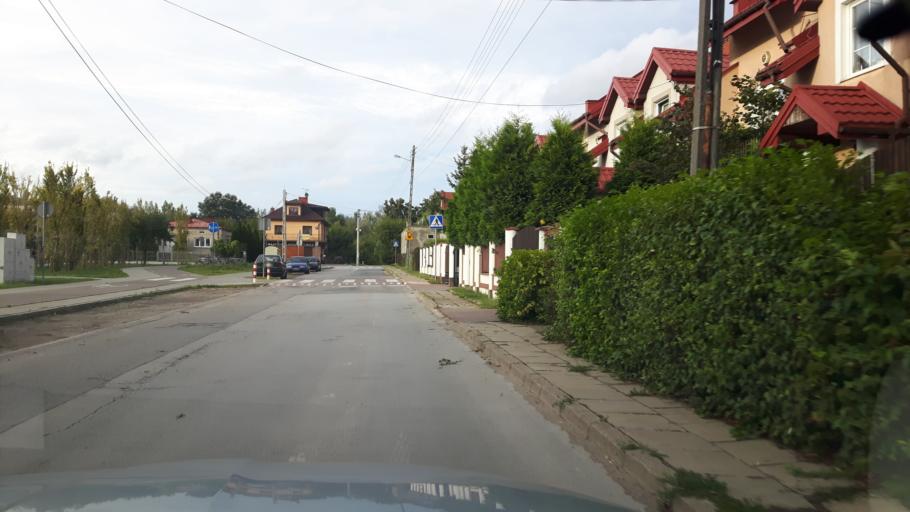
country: PL
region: Masovian Voivodeship
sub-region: Powiat wolominski
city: Marki
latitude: 52.3261
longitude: 21.1103
